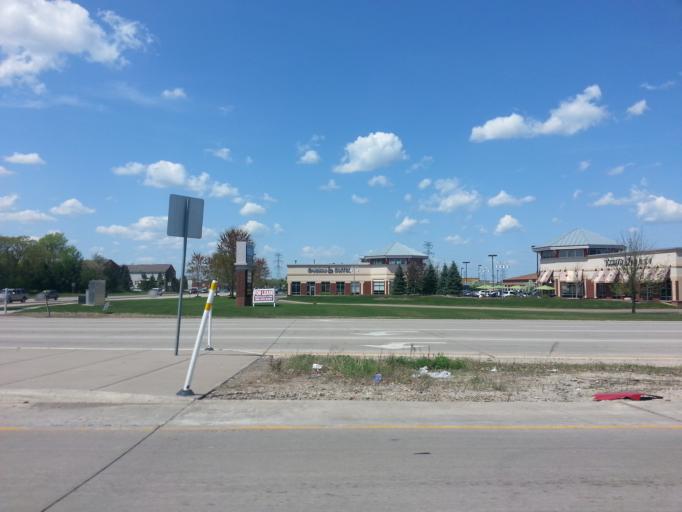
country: US
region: Minnesota
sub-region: Scott County
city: Prior Lake
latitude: 44.7743
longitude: -93.4147
